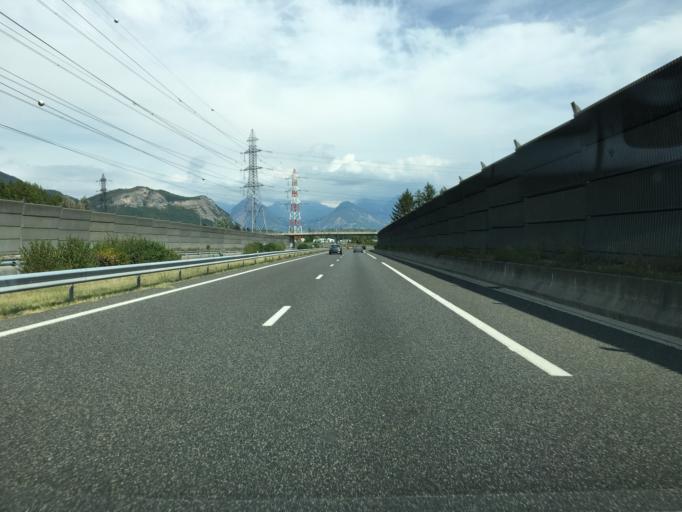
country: FR
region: Rhone-Alpes
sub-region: Departement de l'Isere
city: Allieres-et-Risset
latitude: 45.1058
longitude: 5.6780
